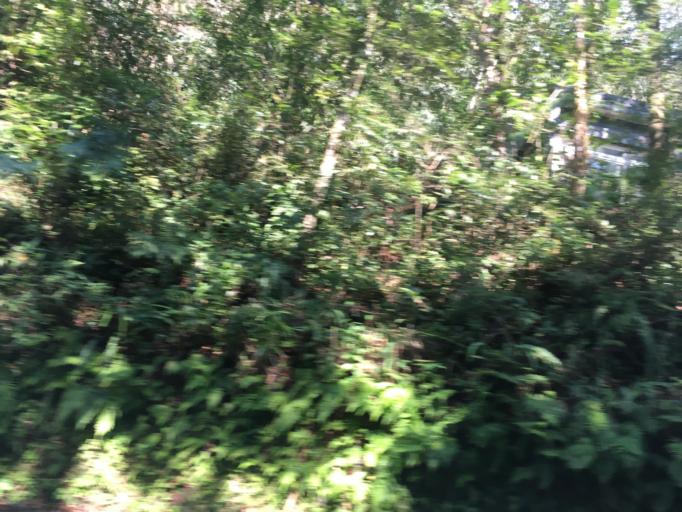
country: TW
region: Taiwan
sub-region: Yilan
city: Yilan
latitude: 24.7575
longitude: 121.5946
